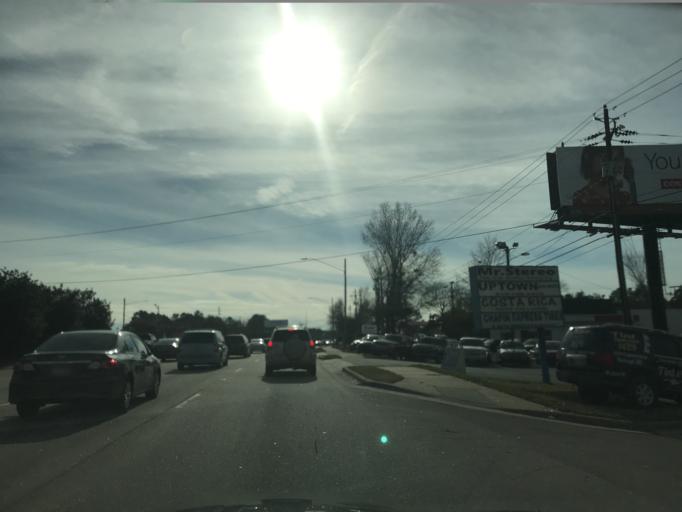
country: US
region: North Carolina
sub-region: Wake County
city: Raleigh
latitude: 35.8262
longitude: -78.5864
